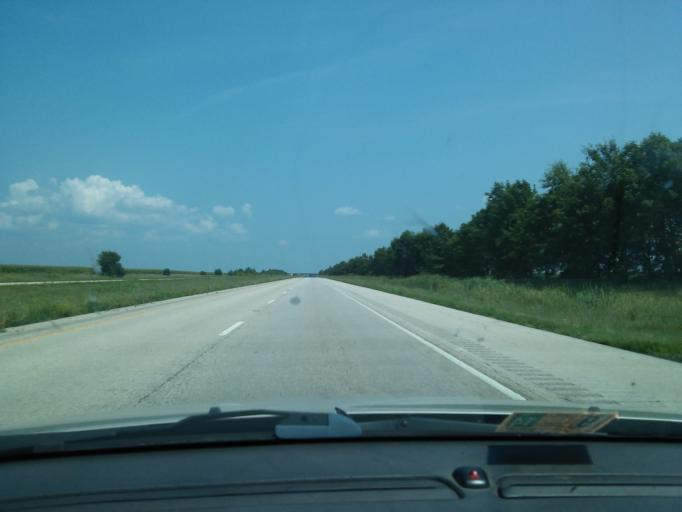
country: US
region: Illinois
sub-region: Sangamon County
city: New Berlin
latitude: 39.7407
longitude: -89.8606
